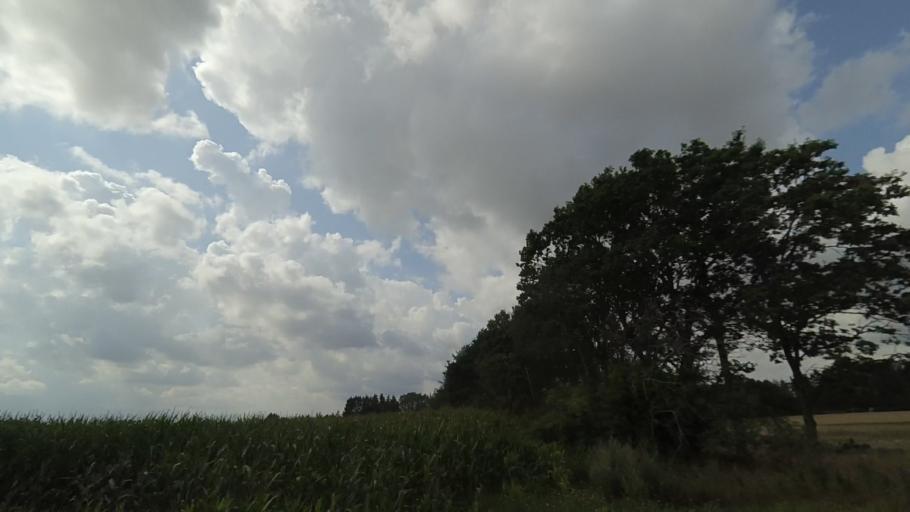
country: DK
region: Central Jutland
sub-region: Norddjurs Kommune
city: Allingabro
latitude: 56.5272
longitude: 10.3164
